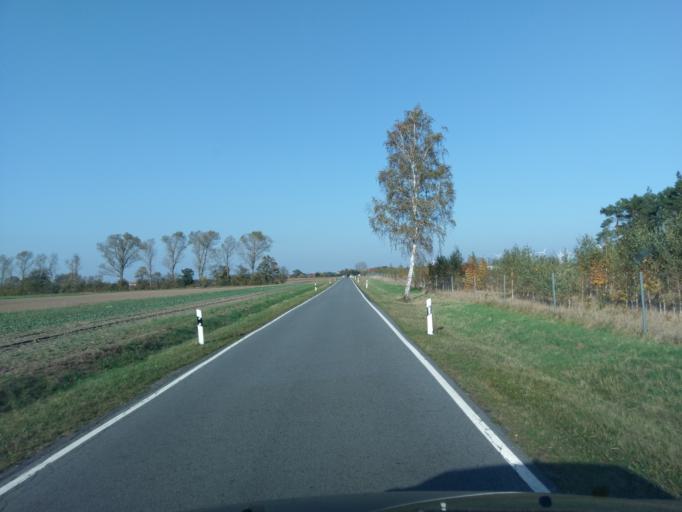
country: DE
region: Brandenburg
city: Muhlberg
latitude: 51.4933
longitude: 13.2770
